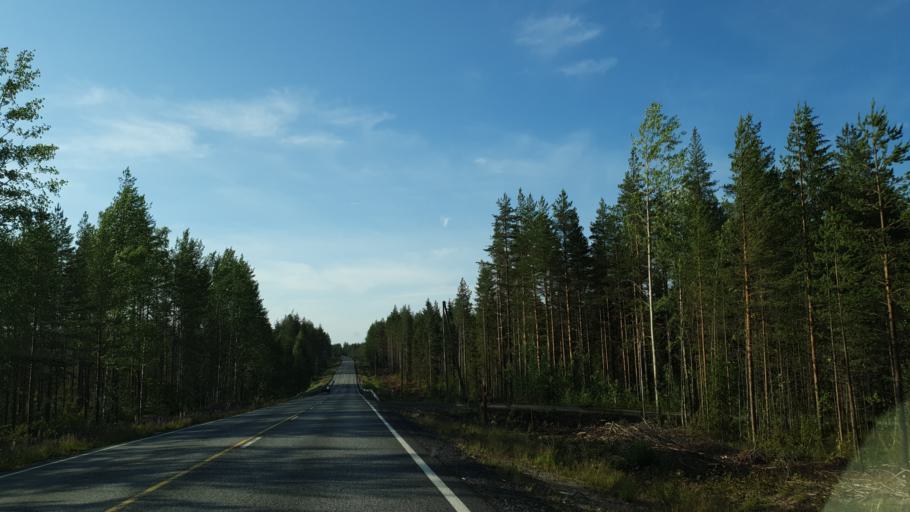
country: FI
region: Kainuu
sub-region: Kehys-Kainuu
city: Kuhmo
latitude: 64.0856
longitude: 29.4835
